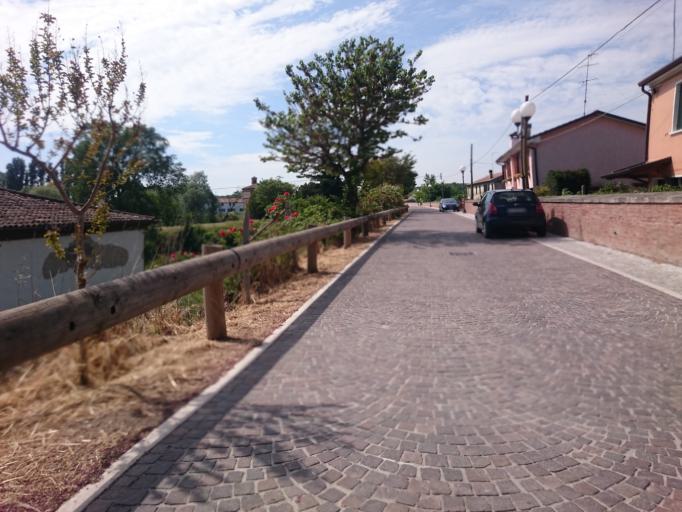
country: IT
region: Emilia-Romagna
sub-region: Provincia di Ferrara
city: Serravalle
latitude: 44.9758
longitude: 12.0724
